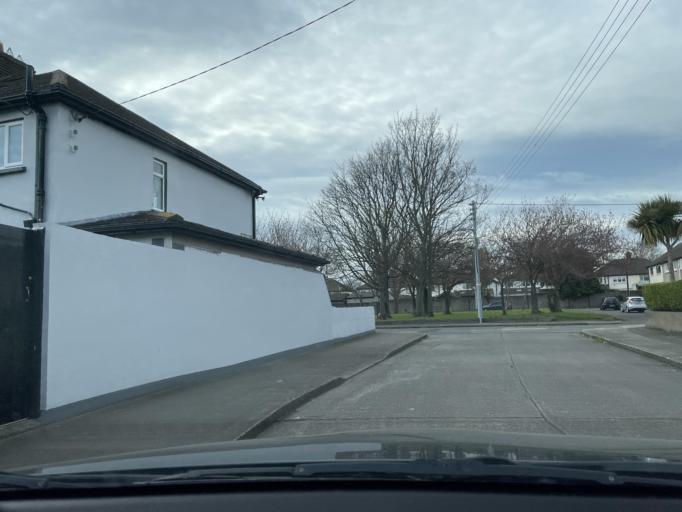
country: IE
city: Donnycarney
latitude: 53.3781
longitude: -6.2105
